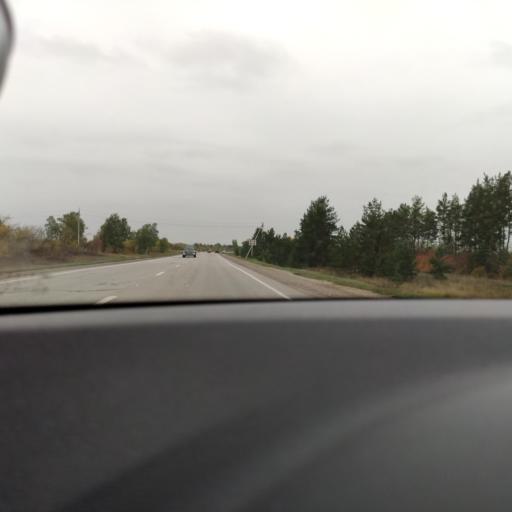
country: RU
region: Samara
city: Mirnyy
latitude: 53.5265
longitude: 50.3125
